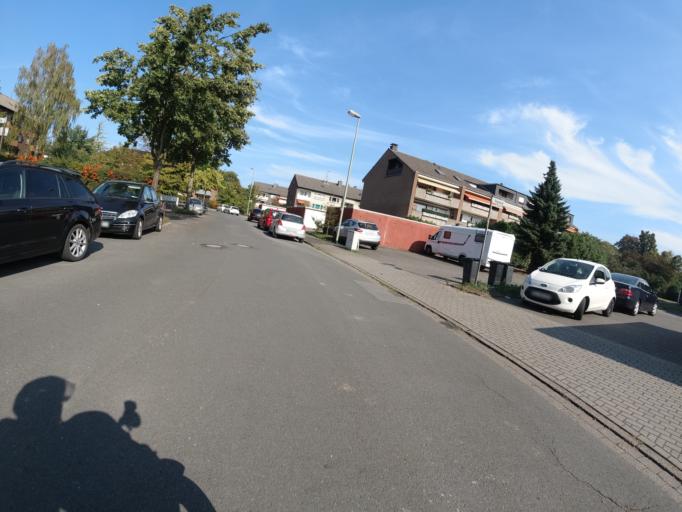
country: DE
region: North Rhine-Westphalia
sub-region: Regierungsbezirk Dusseldorf
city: Hochfeld
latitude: 51.3996
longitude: 6.6921
